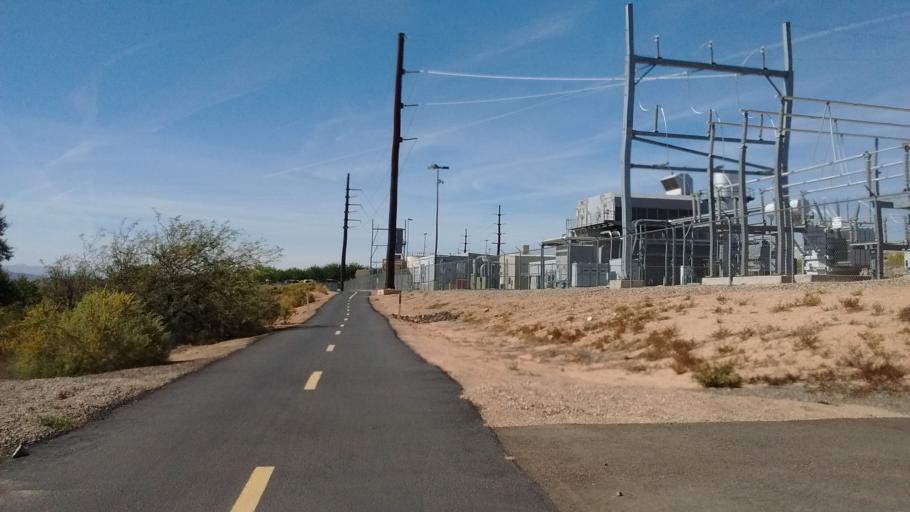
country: US
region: Utah
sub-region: Washington County
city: Washington
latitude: 37.1125
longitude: -113.5144
